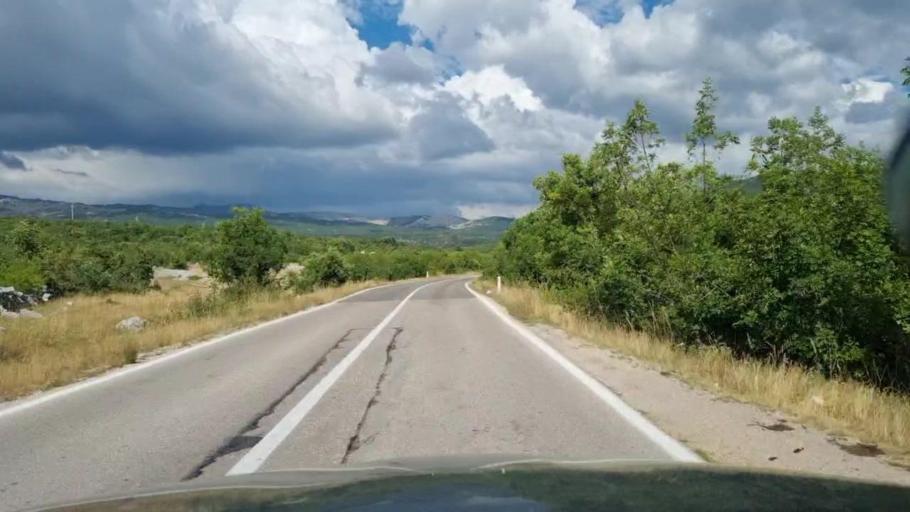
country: BA
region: Federation of Bosnia and Herzegovina
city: Blagaj
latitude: 43.2540
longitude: 17.9902
